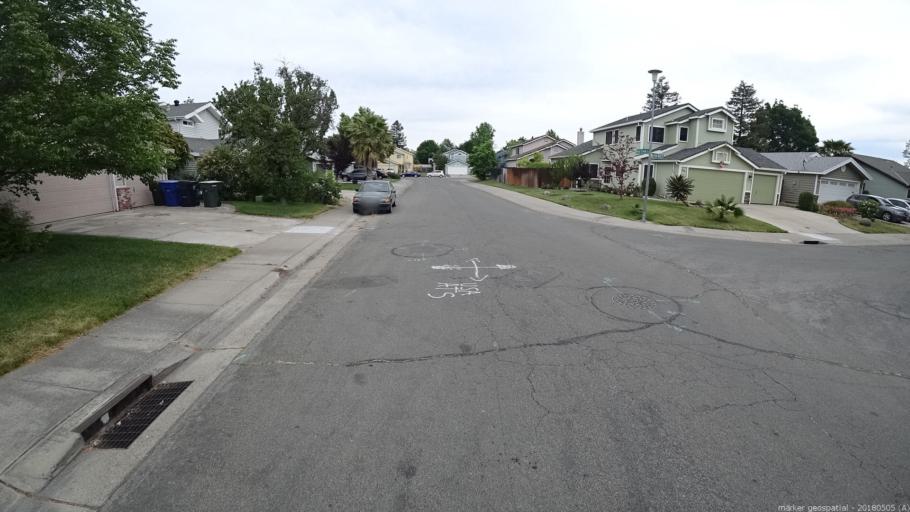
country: US
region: California
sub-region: Sacramento County
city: Rio Linda
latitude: 38.6571
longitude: -121.4469
